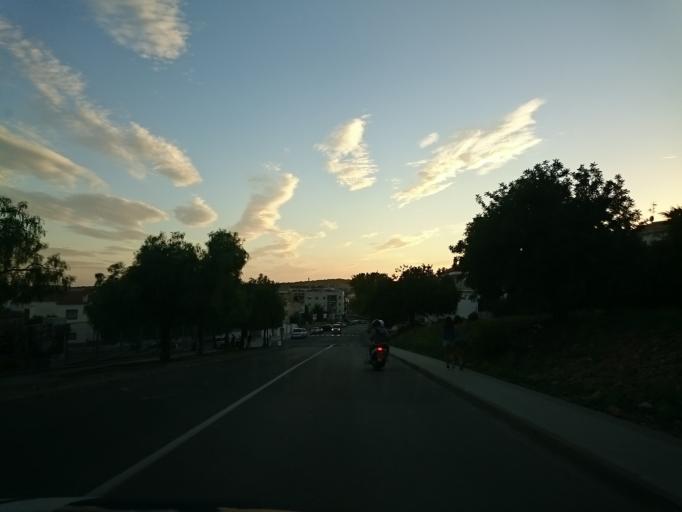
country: ES
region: Catalonia
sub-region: Provincia de Barcelona
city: Sant Pere de Ribes
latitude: 41.2611
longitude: 1.7793
